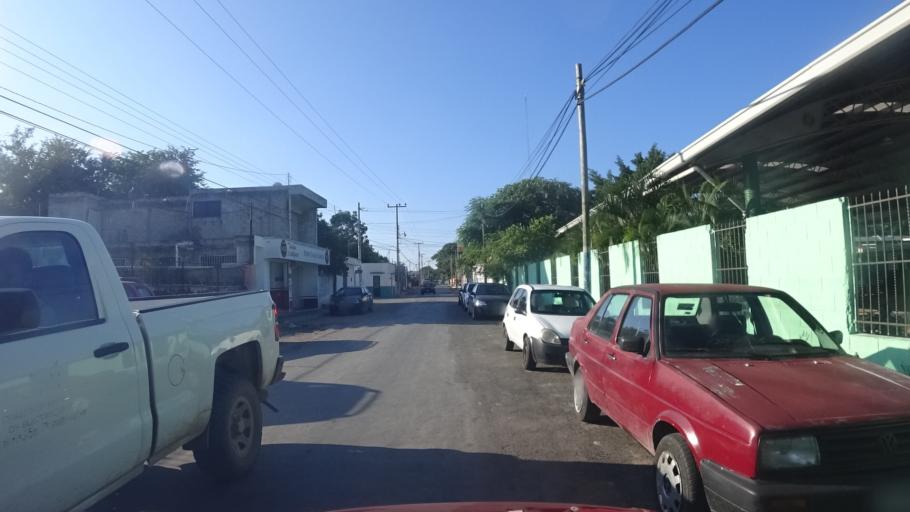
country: MX
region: Yucatan
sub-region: Tizimin
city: Tizimin
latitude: 21.1557
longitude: -88.1510
